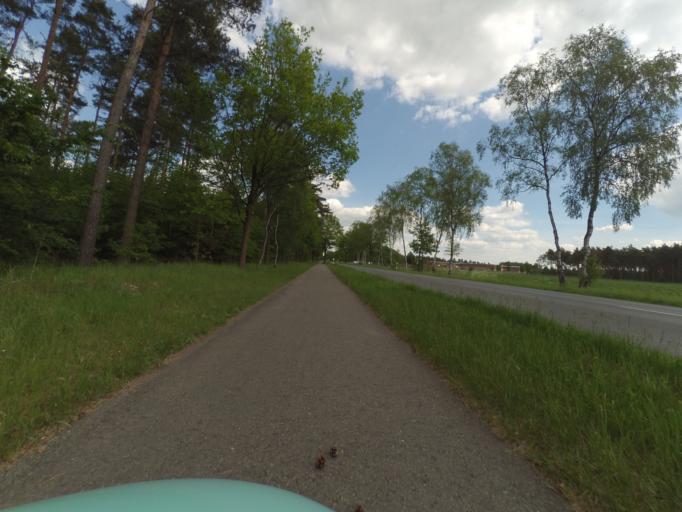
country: DE
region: Lower Saxony
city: Lachendorf
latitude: 52.6069
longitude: 10.2276
